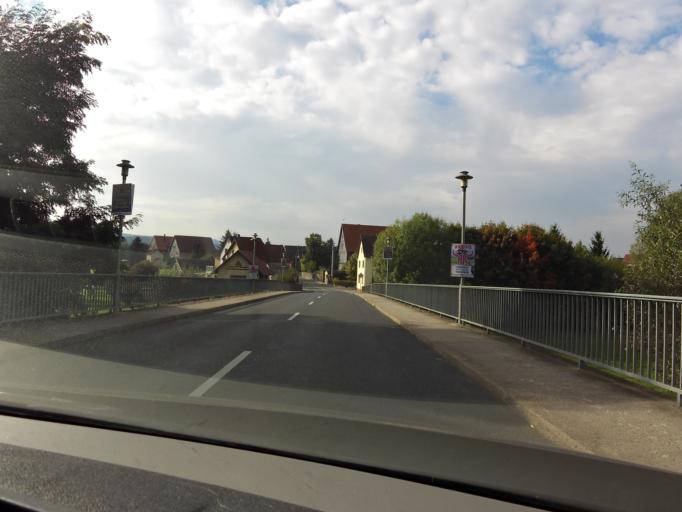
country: DE
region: Thuringia
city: Breitungen
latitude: 50.7543
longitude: 10.3414
